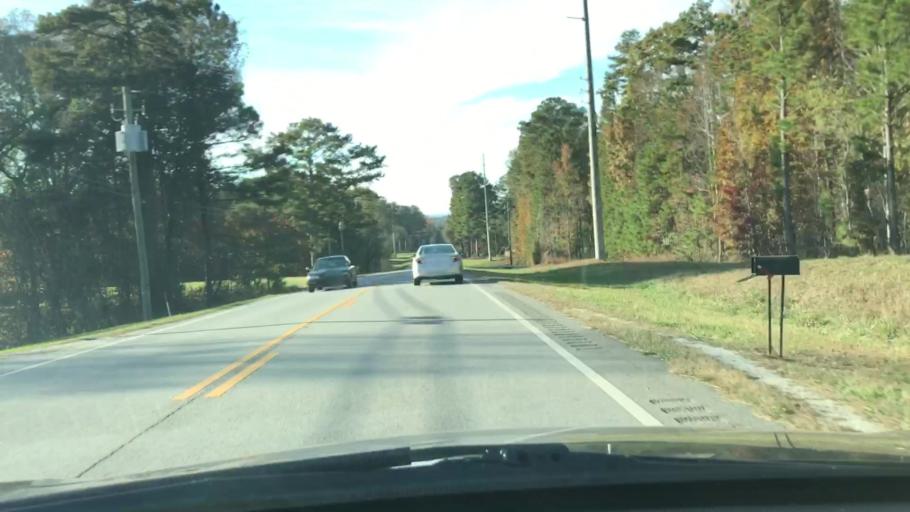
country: US
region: Alabama
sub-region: Cleburne County
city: Heflin
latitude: 33.6508
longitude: -85.5185
